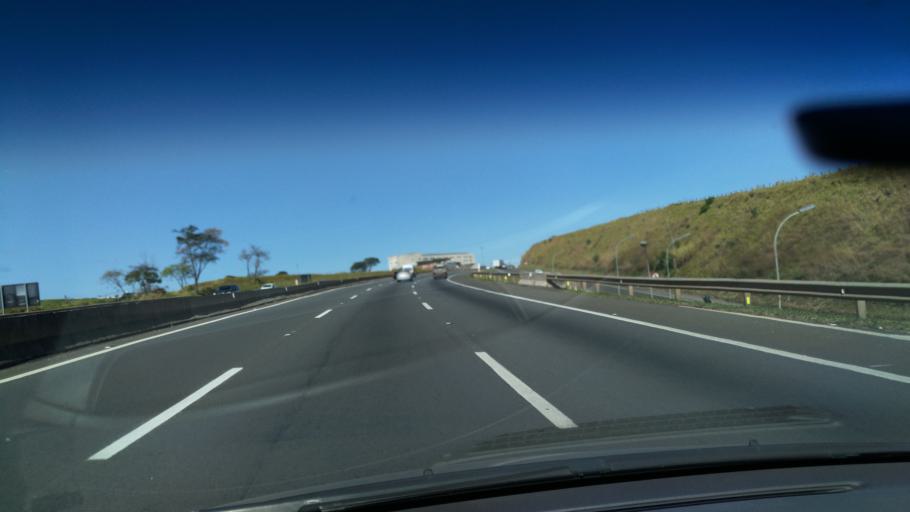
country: BR
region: Sao Paulo
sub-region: Campinas
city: Campinas
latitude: -22.8274
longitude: -47.0344
